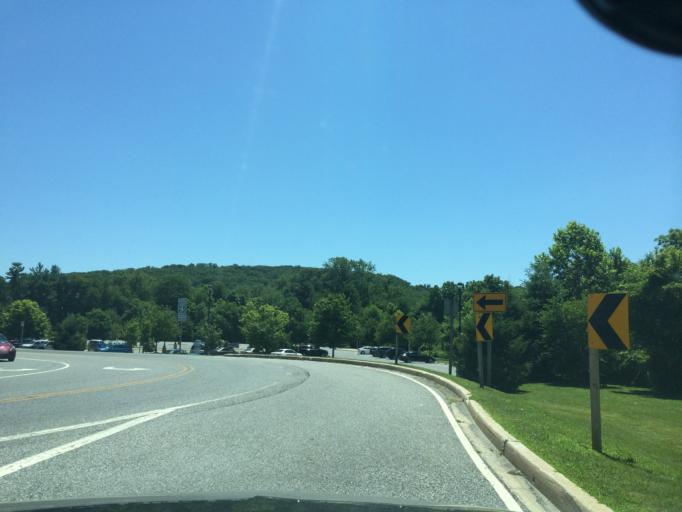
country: US
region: Maryland
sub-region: Baltimore County
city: Mays Chapel
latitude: 39.4188
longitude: -76.6697
